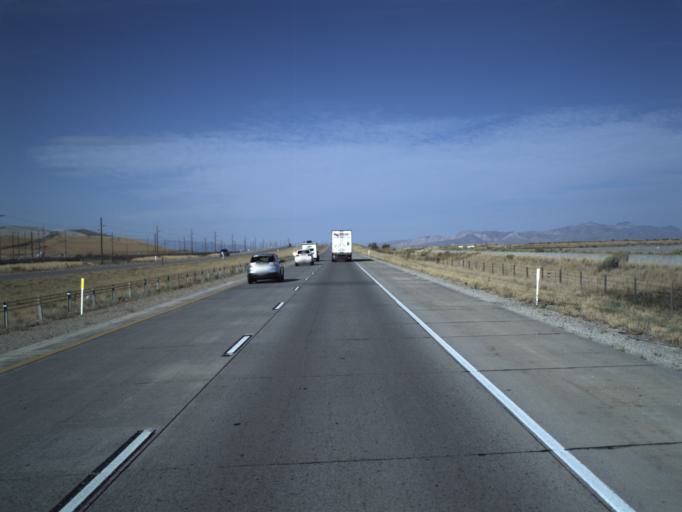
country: US
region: Utah
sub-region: Salt Lake County
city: Magna
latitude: 40.7710
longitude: -112.1305
